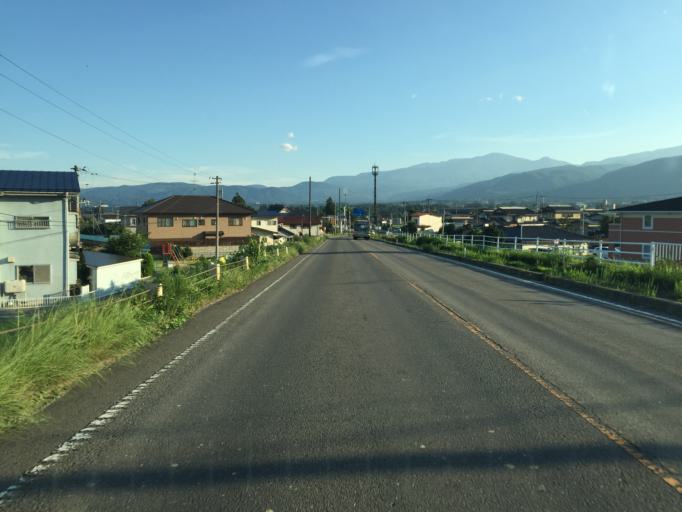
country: JP
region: Fukushima
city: Fukushima-shi
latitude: 37.7717
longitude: 140.3855
